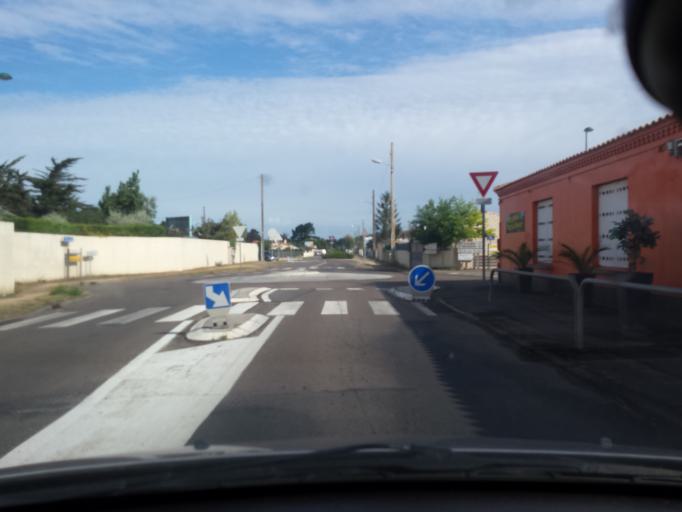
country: FR
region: Pays de la Loire
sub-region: Departement de la Vendee
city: Olonne-sur-Mer
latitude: 46.5461
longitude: -1.8037
